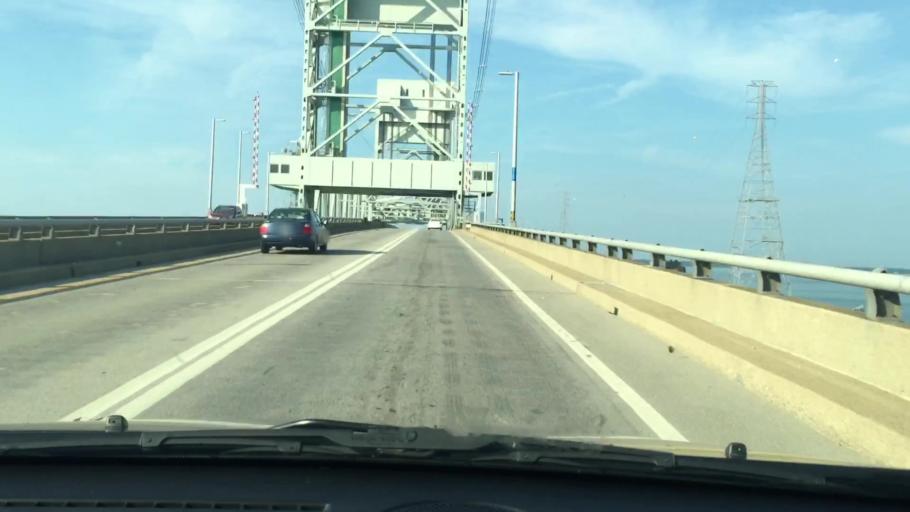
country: US
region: Virginia
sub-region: City of Newport News
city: Newport News
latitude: 37.0041
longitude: -76.4674
